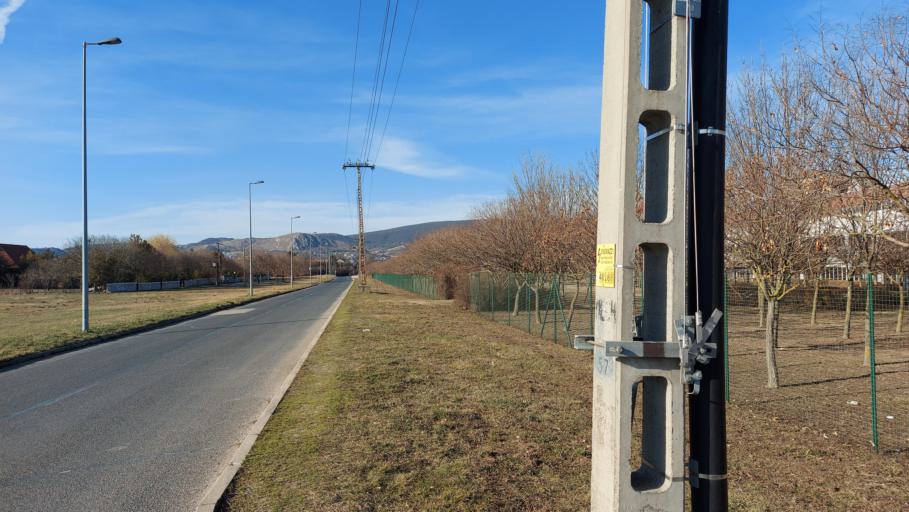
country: HU
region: Pest
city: Budaors
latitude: 47.4439
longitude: 18.9597
